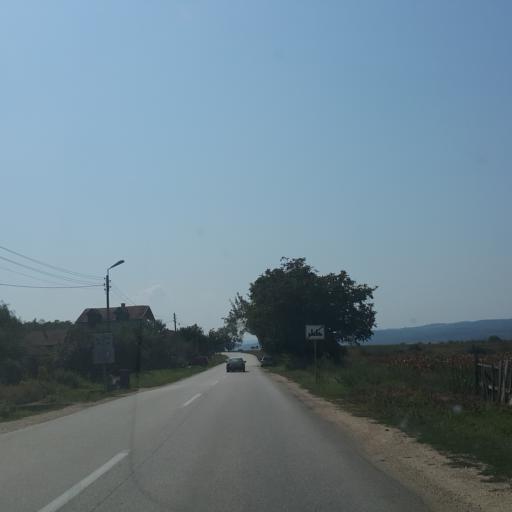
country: RS
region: Central Serbia
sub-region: Zajecarski Okrug
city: Knjazevac
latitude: 43.6797
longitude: 22.2905
